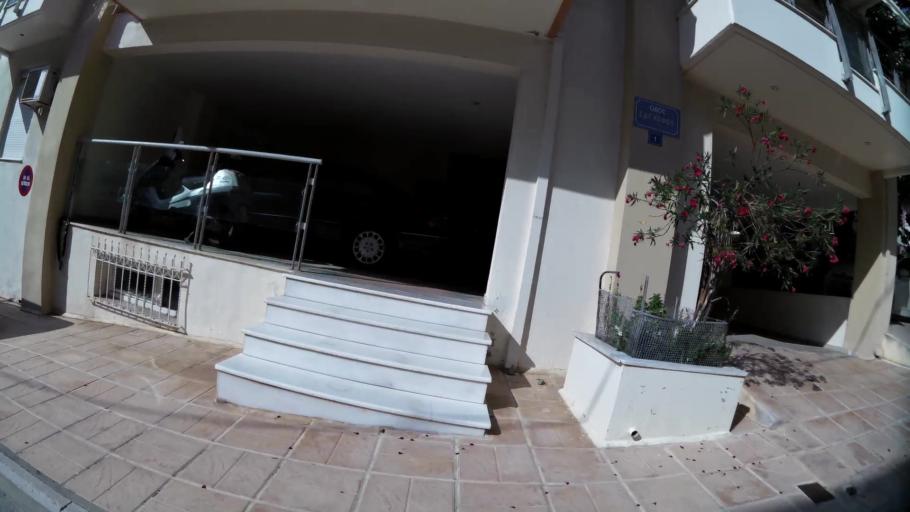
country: GR
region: Central Macedonia
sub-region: Nomos Thessalonikis
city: Sykies
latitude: 40.6584
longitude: 22.9584
